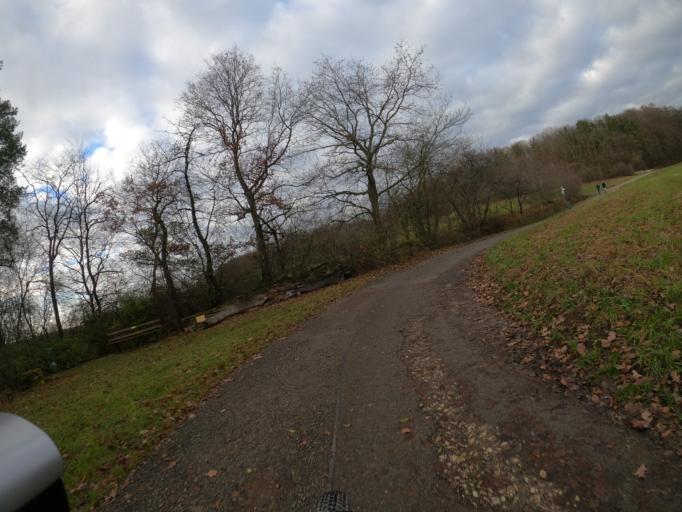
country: DE
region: Baden-Wuerttemberg
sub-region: Regierungsbezirk Stuttgart
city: Notzingen
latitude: 48.6760
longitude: 9.4675
